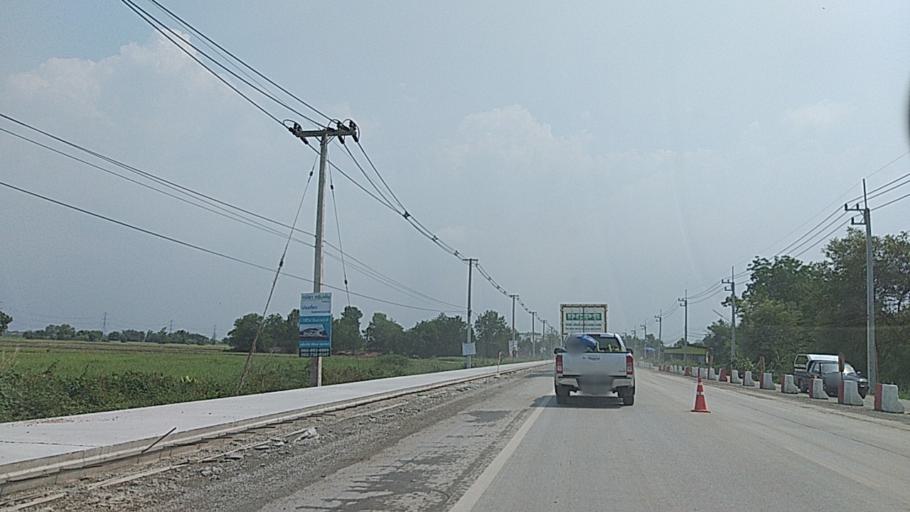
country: TH
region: Chon Buri
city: Phanat Nikhom
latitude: 13.4116
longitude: 101.1890
